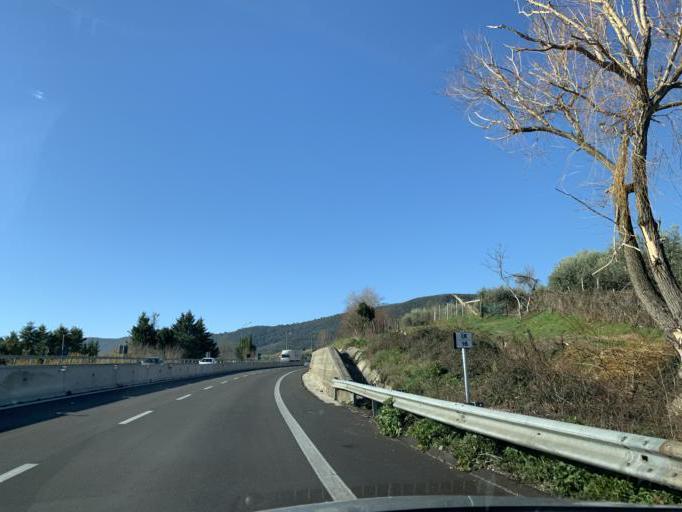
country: IT
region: Umbria
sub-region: Provincia di Terni
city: Narni Scalo
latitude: 42.5421
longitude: 12.5170
